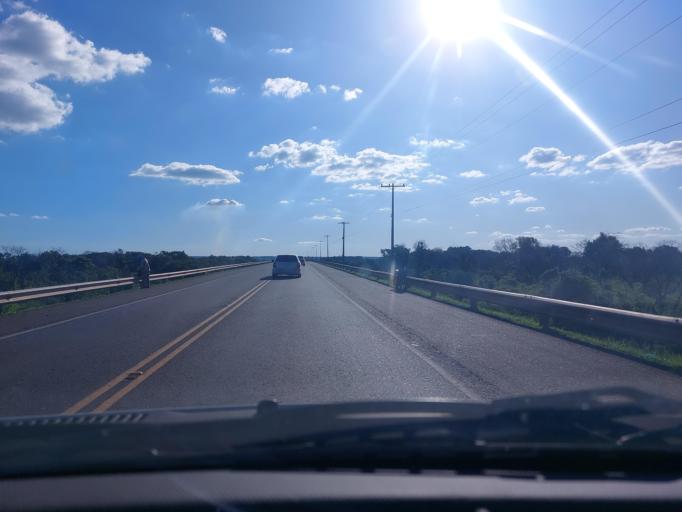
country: PY
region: Cordillera
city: Arroyos y Esteros
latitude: -25.0470
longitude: -57.0490
